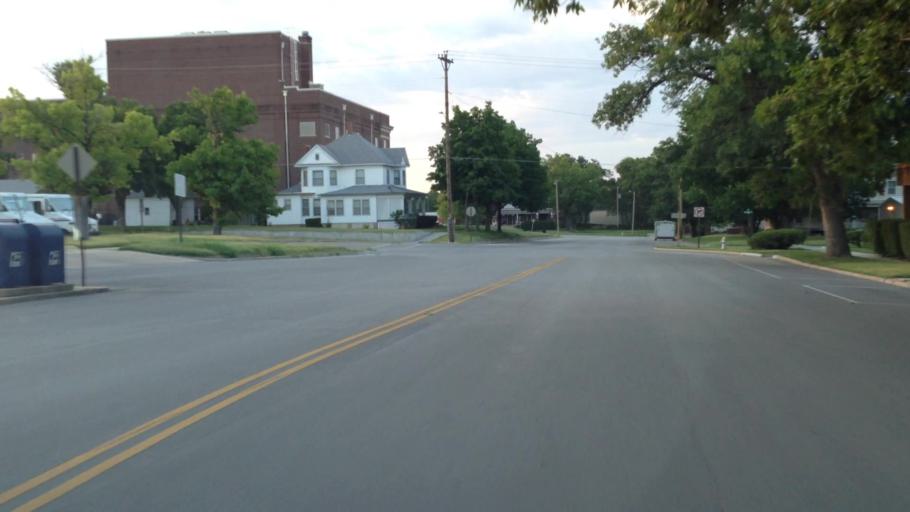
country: US
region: Kansas
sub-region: Montgomery County
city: Independence
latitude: 37.2260
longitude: -95.7052
